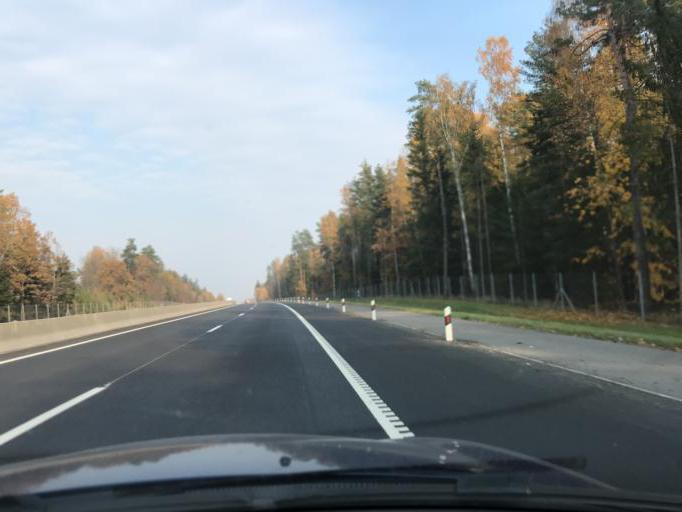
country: BY
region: Grodnenskaya
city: Shchuchin
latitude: 53.6691
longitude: 24.8279
